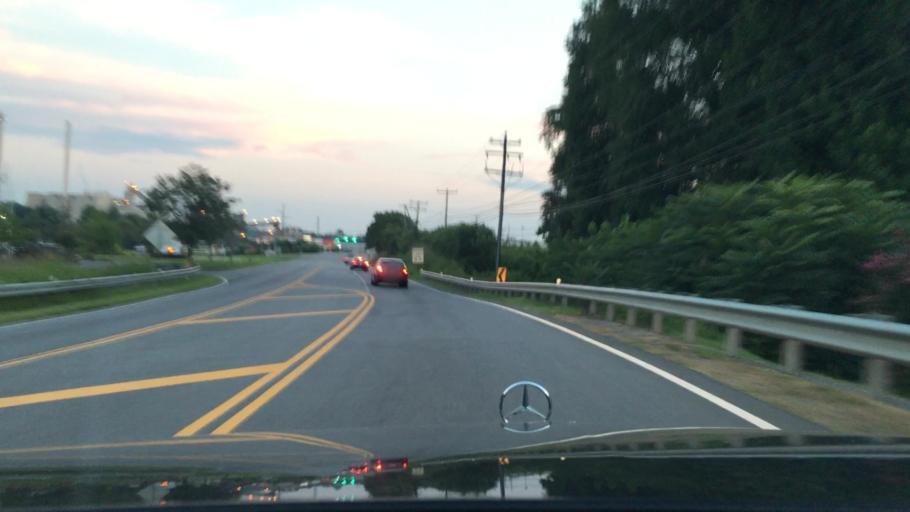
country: US
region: Virginia
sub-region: Campbell County
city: Altavista
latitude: 37.1231
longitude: -79.2736
